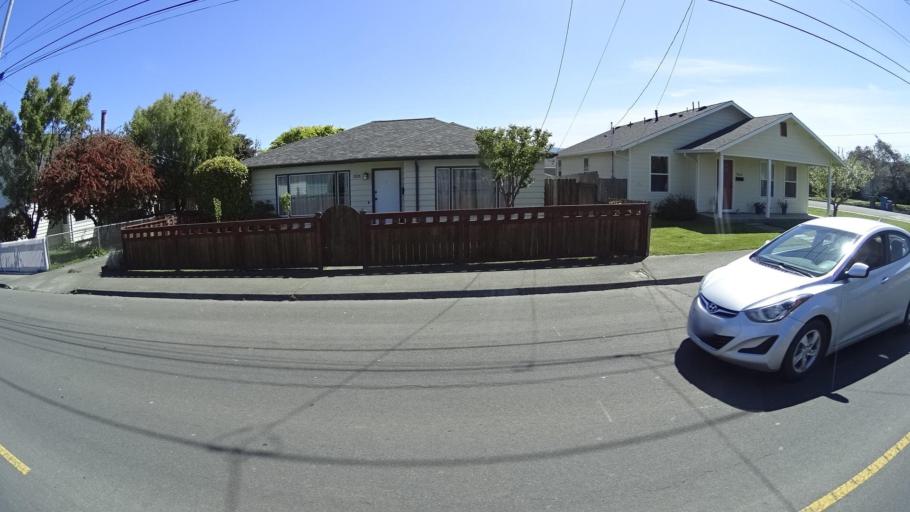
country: US
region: California
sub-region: Humboldt County
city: Eureka
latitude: 40.7954
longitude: -124.1482
